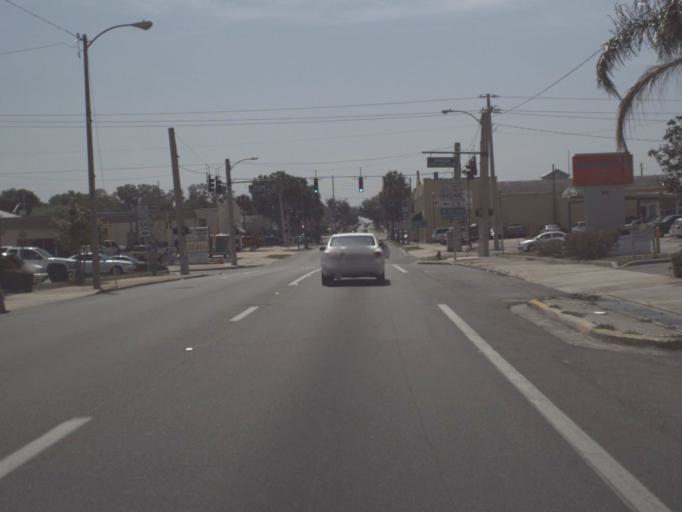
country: US
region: Florida
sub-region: Lake County
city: Eustis
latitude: 28.8533
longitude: -81.6857
